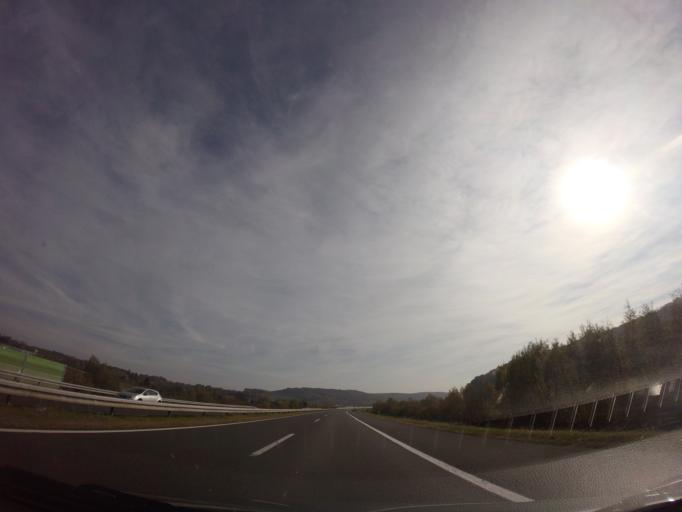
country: HR
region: Varazdinska
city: Remetinec
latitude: 46.0781
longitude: 16.2916
